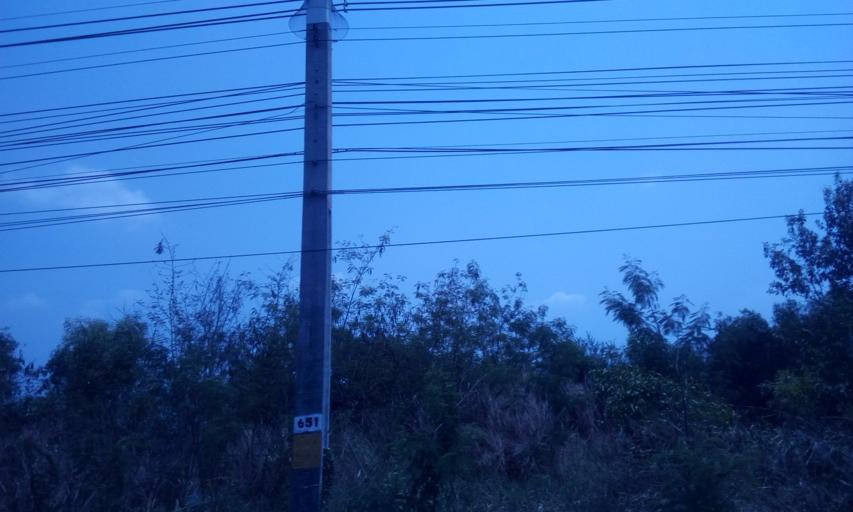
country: TH
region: Chachoengsao
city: Bang Nam Priao
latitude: 13.8054
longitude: 101.0534
